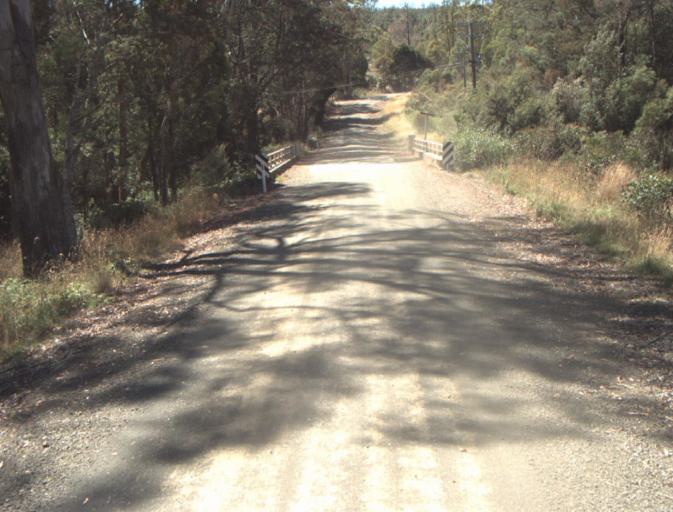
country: AU
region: Tasmania
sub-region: Launceston
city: Newstead
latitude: -41.3428
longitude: 147.3643
